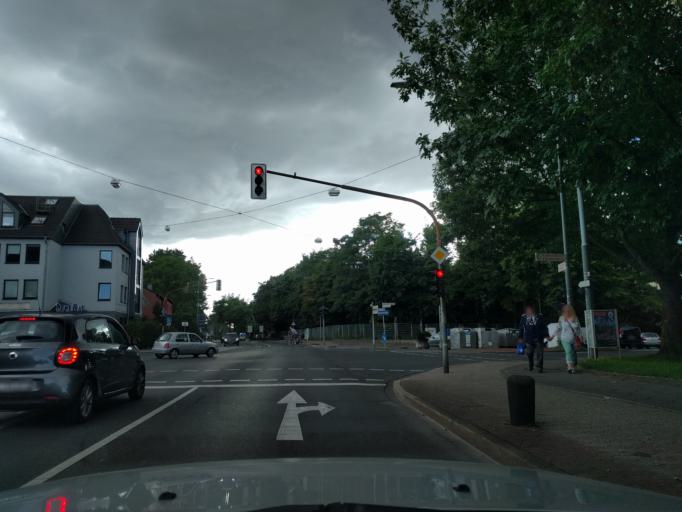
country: DE
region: North Rhine-Westphalia
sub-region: Regierungsbezirk Dusseldorf
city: Ratingen
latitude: 51.2943
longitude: 6.8541
